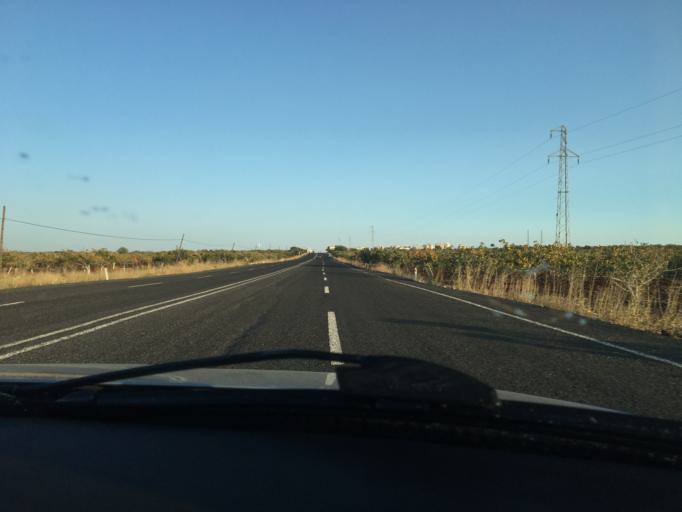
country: TR
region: Sanliurfa
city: Halfeti
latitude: 37.2361
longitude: 37.9278
